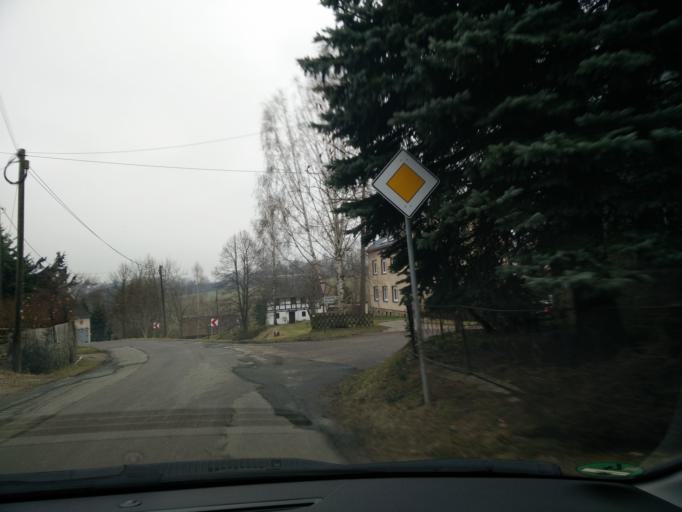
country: DE
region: Saxony
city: Lunzenau
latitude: 50.9742
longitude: 12.7727
